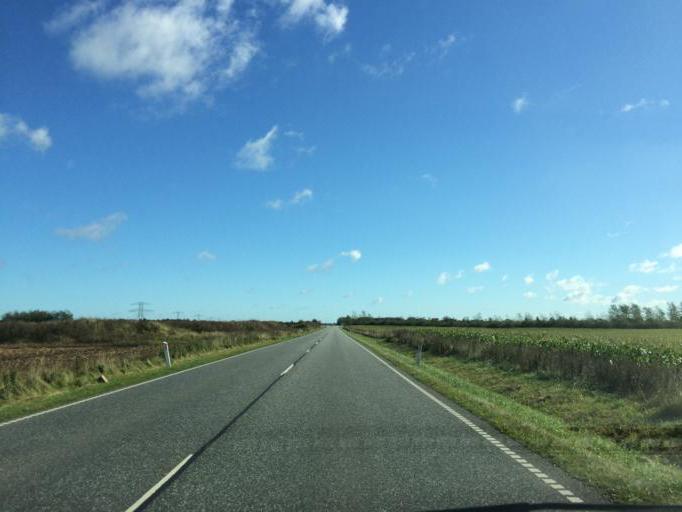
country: DK
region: Central Jutland
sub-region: Holstebro Kommune
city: Vinderup
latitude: 56.3982
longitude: 8.8953
